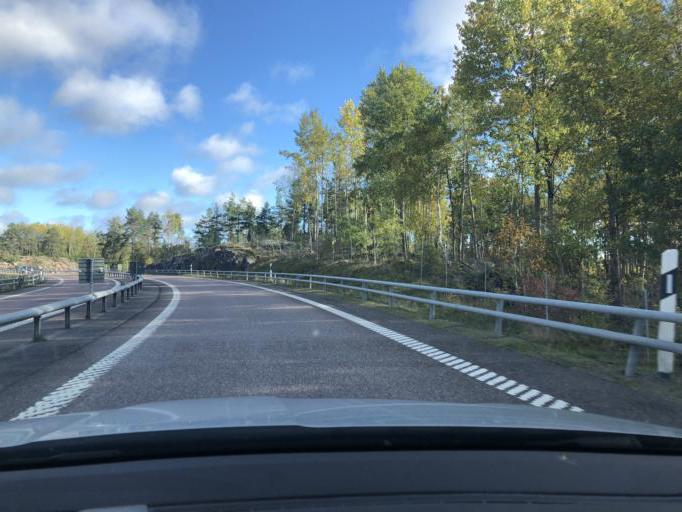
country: SE
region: Soedermanland
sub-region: Strangnas Kommun
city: Strangnas
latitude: 59.3664
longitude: 16.9526
